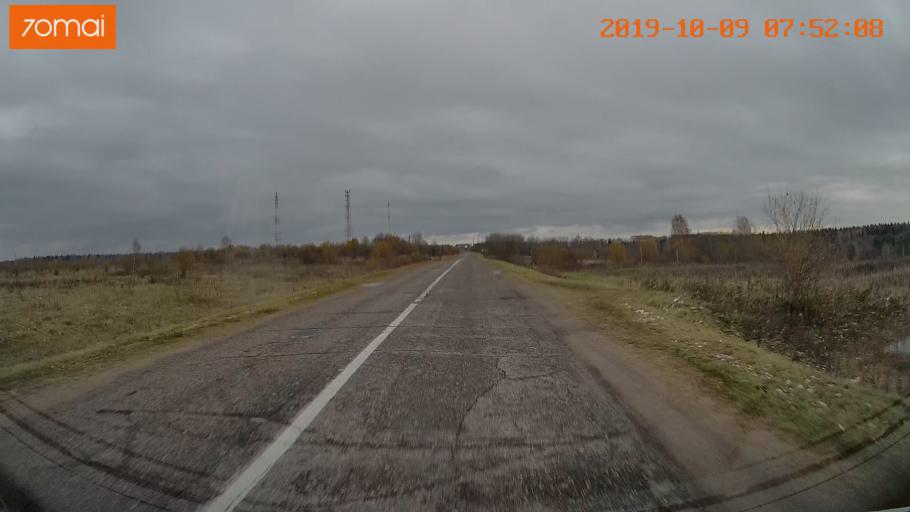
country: RU
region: Jaroslavl
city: Kukoboy
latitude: 58.6887
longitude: 39.8829
